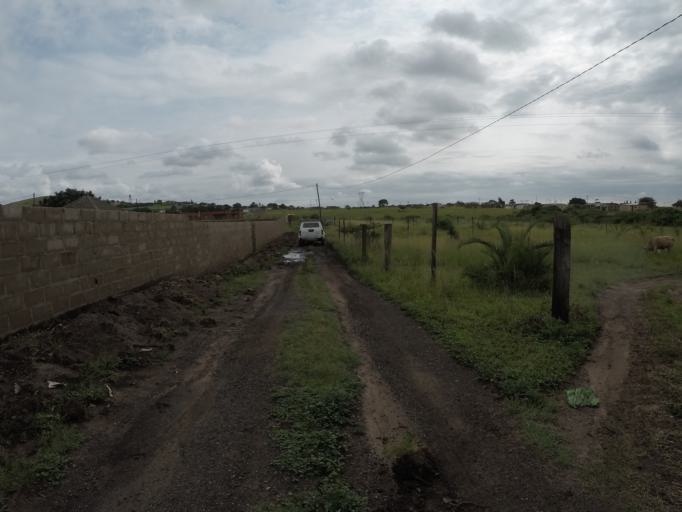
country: ZA
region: KwaZulu-Natal
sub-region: uThungulu District Municipality
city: Empangeni
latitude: -28.7124
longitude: 31.8643
